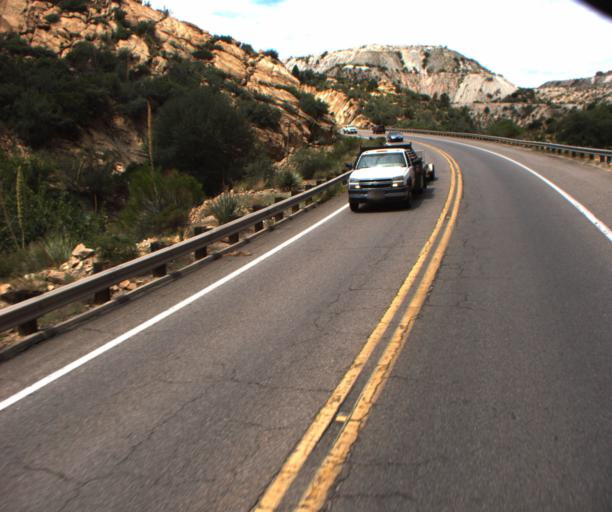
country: US
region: Arizona
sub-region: Gila County
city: Miami
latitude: 33.3810
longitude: -110.9037
